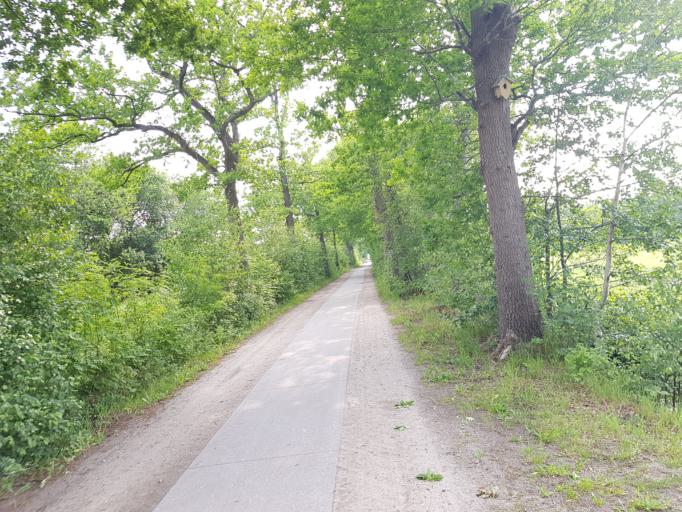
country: NL
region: Friesland
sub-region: Gemeente Heerenveen
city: Jubbega
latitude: 53.0349
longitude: 6.1191
